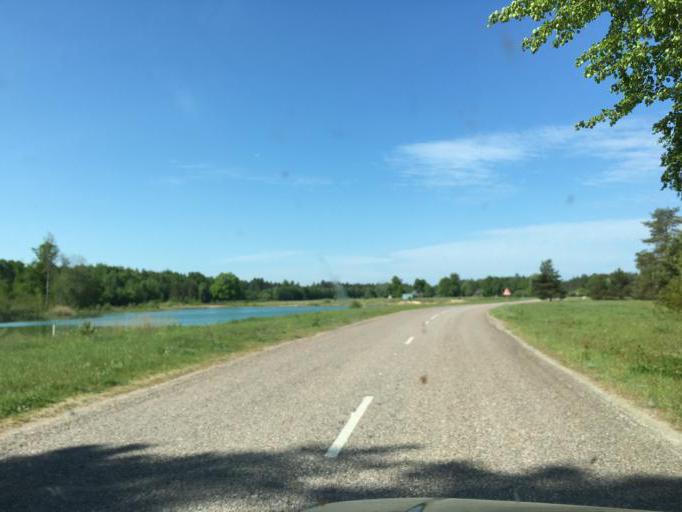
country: LV
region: Ventspils
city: Ventspils
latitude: 57.4828
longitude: 21.7699
